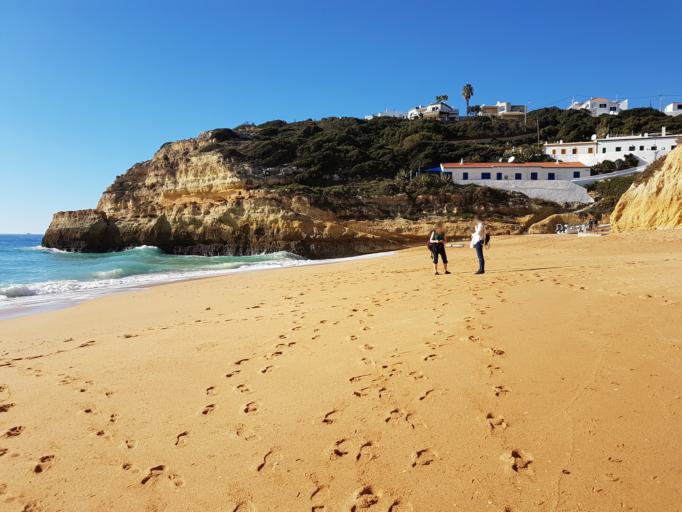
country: PT
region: Faro
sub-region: Lagoa
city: Carvoeiro
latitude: 37.0873
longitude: -8.4255
